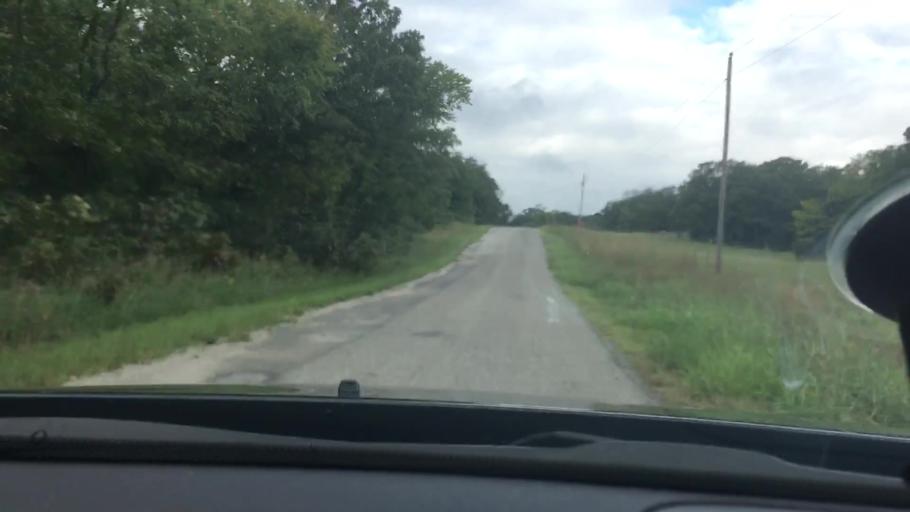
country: US
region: Oklahoma
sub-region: Pontotoc County
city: Byng
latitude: 34.8180
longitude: -96.5448
